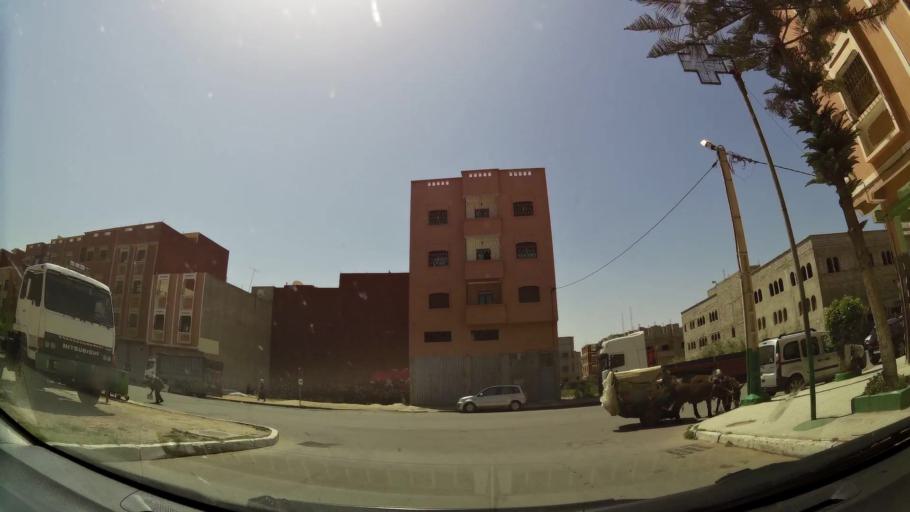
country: MA
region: Souss-Massa-Draa
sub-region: Inezgane-Ait Mellou
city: Inezgane
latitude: 30.3336
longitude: -9.4999
